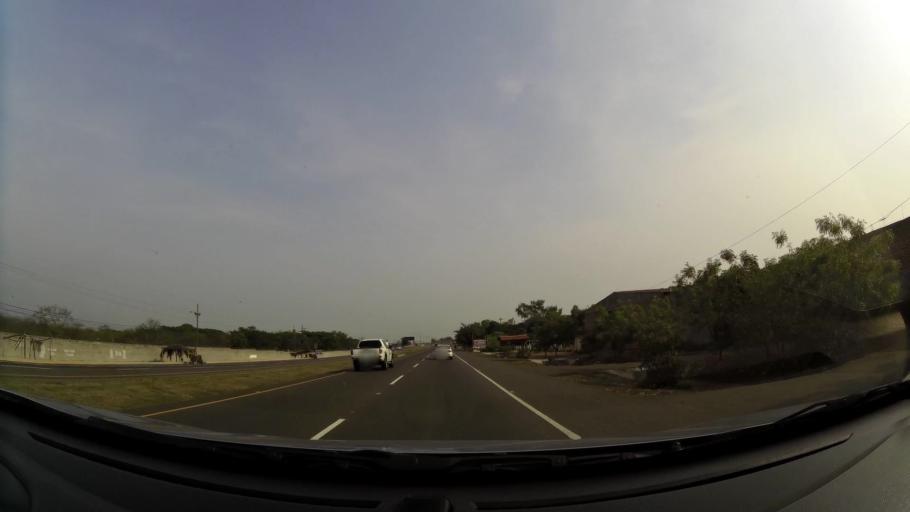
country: HN
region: La Paz
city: Yarumela
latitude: 14.3735
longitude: -87.6065
